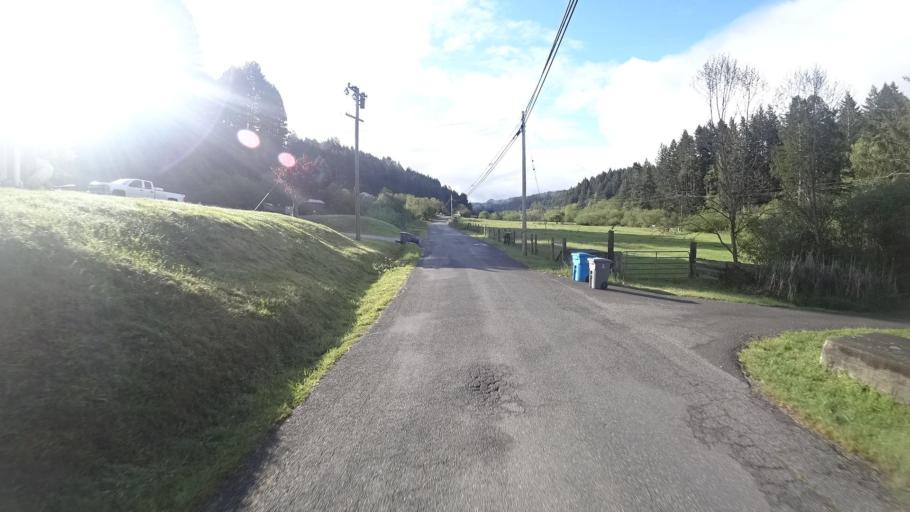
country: US
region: California
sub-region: Humboldt County
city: Arcata
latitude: 40.8960
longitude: -124.0444
